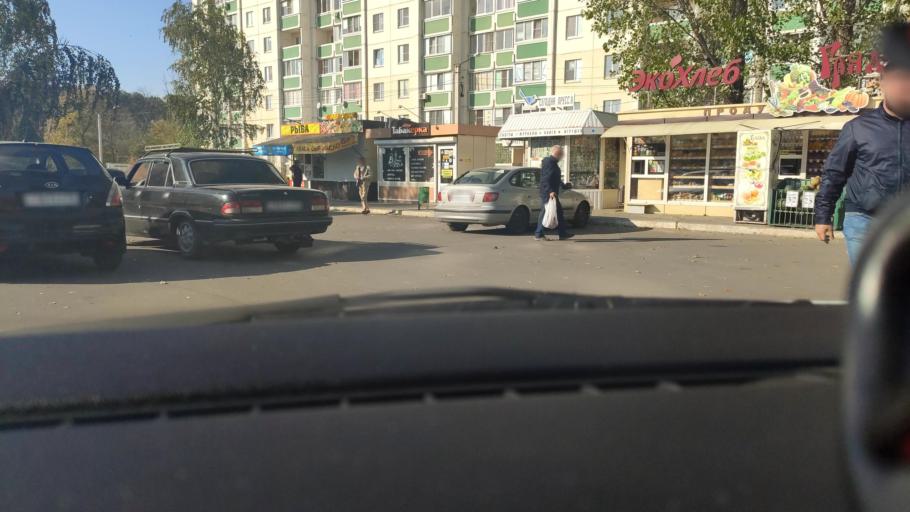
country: RU
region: Voronezj
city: Pridonskoy
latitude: 51.6254
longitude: 39.0683
